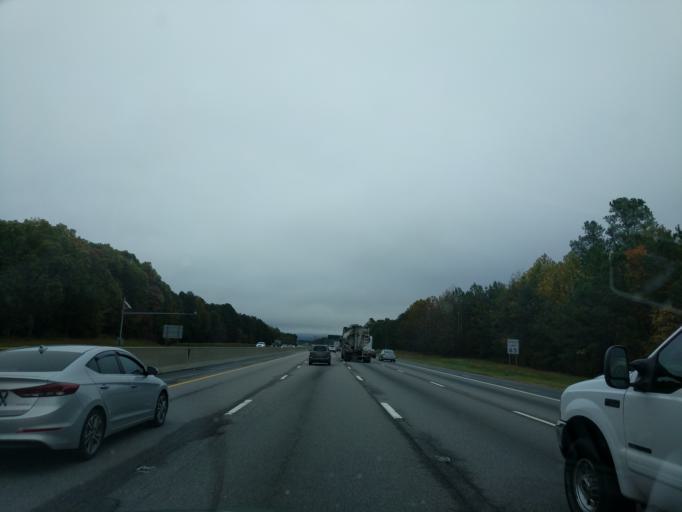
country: US
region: North Carolina
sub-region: Alamance County
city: Mebane
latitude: 36.0754
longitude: -79.1936
